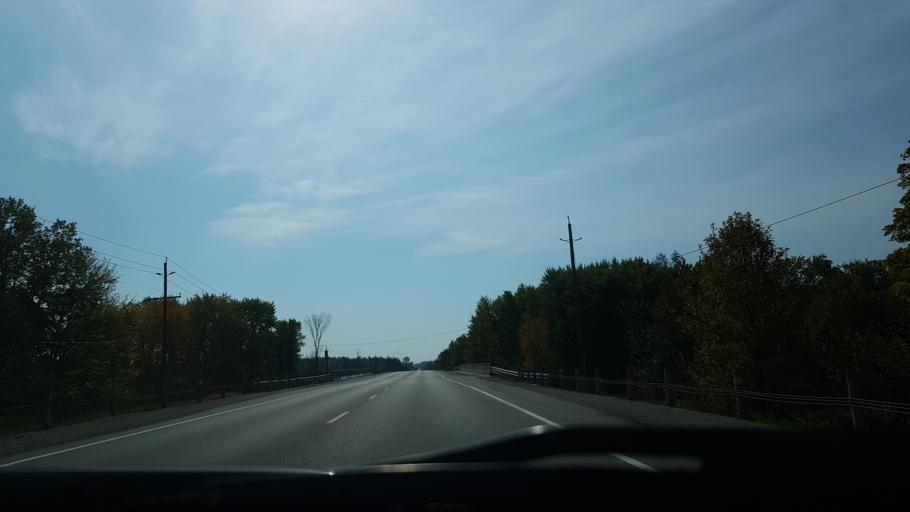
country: CA
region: Ontario
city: Orillia
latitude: 44.7149
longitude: -79.2821
